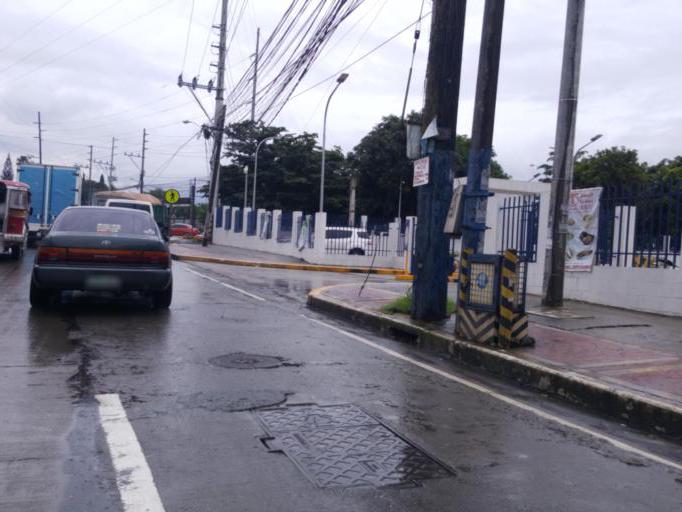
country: PH
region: Calabarzon
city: Bagong Pagasa
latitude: 14.7309
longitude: 121.0468
